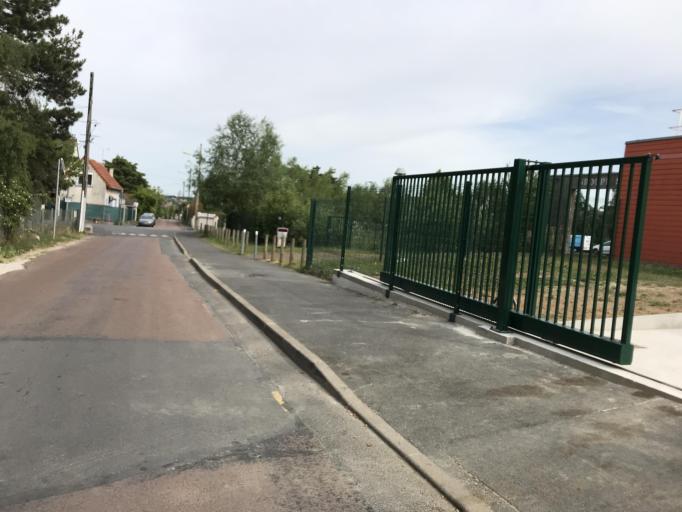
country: FR
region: Ile-de-France
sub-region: Departement de l'Essonne
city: Montlhery
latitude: 48.6338
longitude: 2.2841
